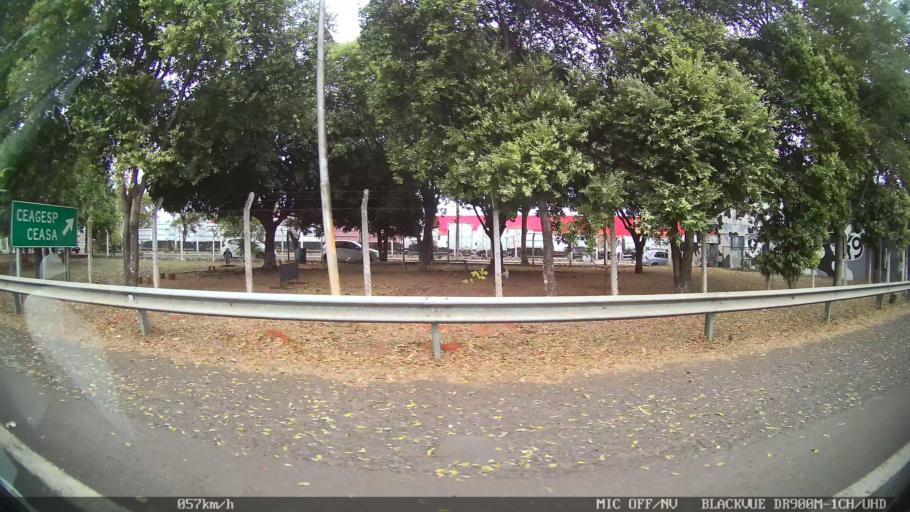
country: BR
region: Sao Paulo
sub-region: Sao Jose Do Rio Preto
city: Sao Jose do Rio Preto
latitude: -20.8226
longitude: -49.4223
